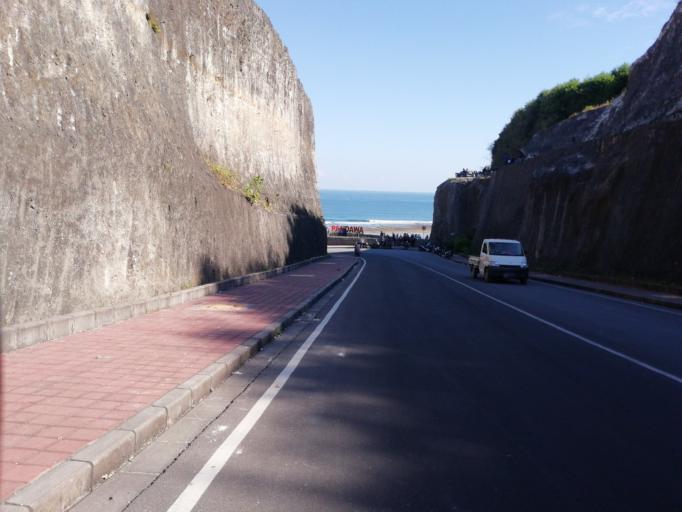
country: ID
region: Bali
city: Bualu
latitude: -8.8423
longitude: 115.1855
